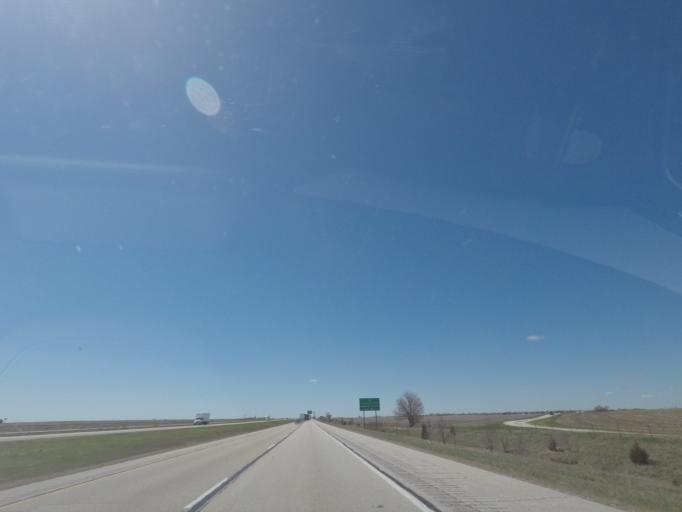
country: US
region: Illinois
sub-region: McLean County
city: Normal
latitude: 40.5474
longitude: -88.9257
